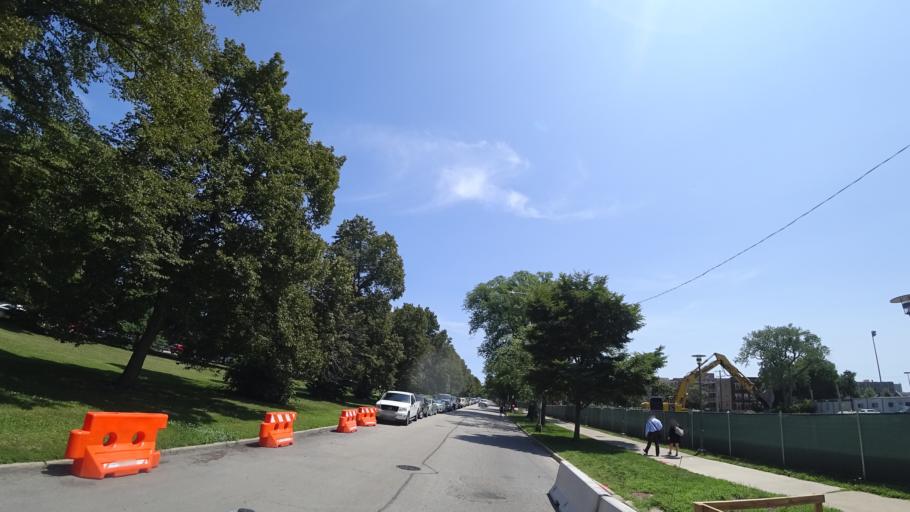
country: US
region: Illinois
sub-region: Cook County
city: Chicago
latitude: 41.7860
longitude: -87.5960
